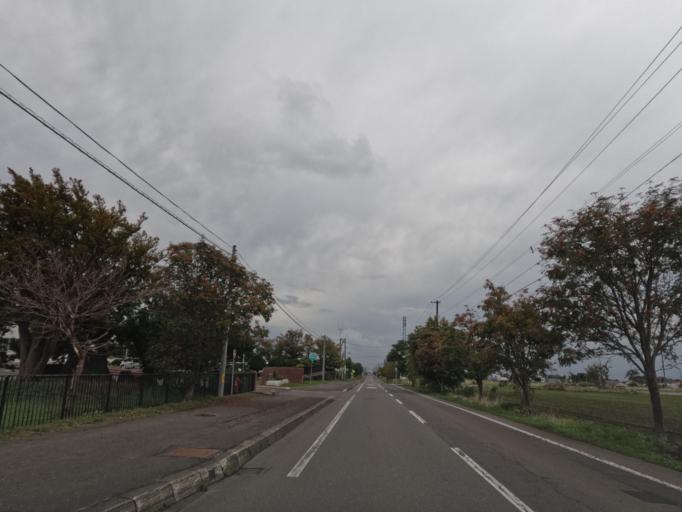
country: JP
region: Hokkaido
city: Date
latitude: 42.4293
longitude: 140.9093
